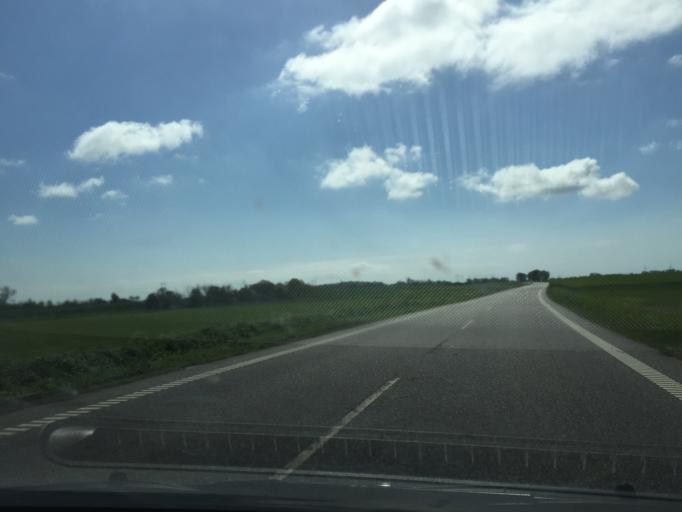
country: DK
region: Zealand
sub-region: Lolland Kommune
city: Rodby
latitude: 54.7095
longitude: 11.4125
